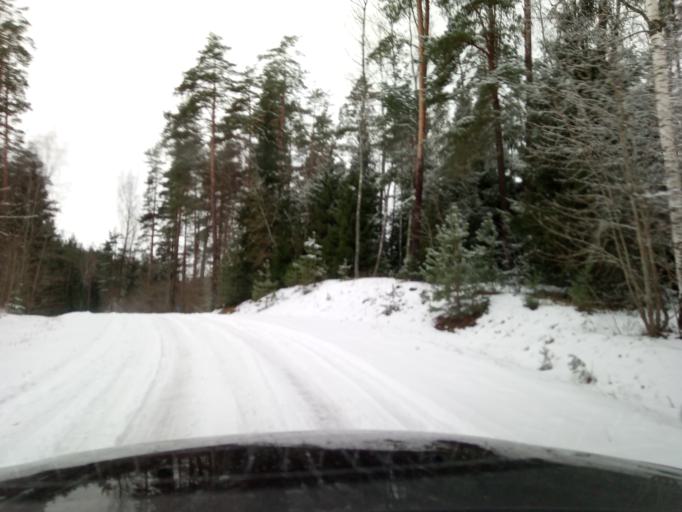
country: LT
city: Zarasai
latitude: 55.6780
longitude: 25.9924
